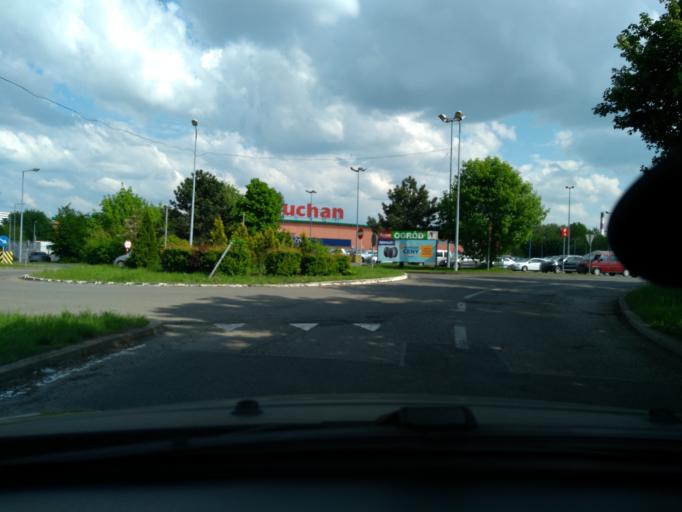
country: PL
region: Silesian Voivodeship
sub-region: Chorzow
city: Chorzow
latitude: 50.2753
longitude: 18.9650
